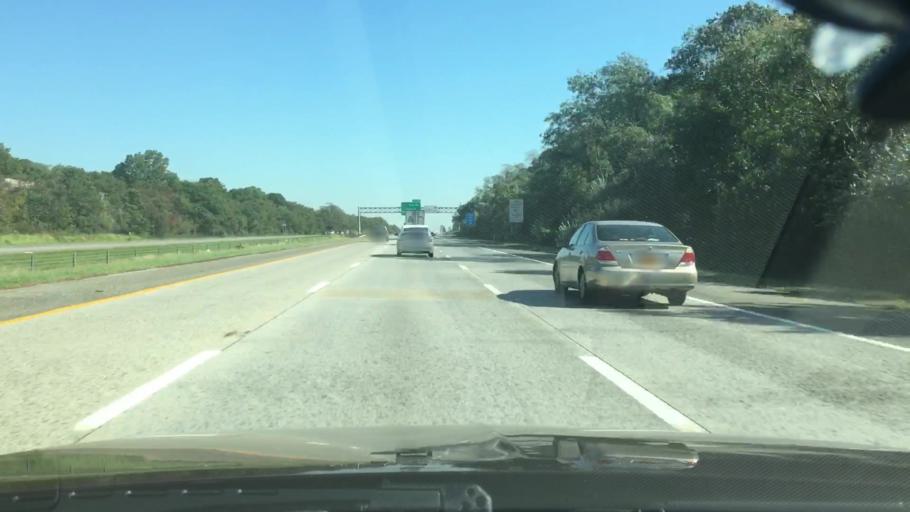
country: US
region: New York
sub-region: Suffolk County
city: Gordon Heights
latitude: 40.8256
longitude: -72.9561
